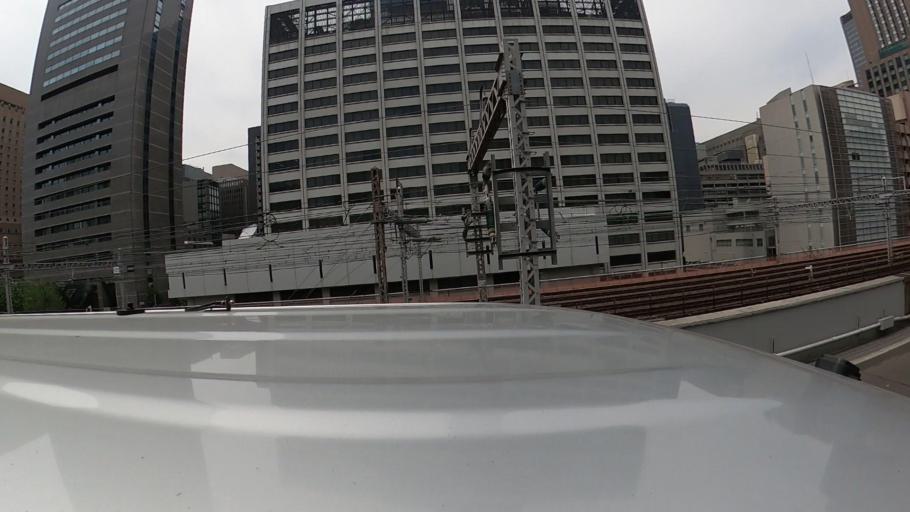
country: JP
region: Tokyo
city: Tokyo
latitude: 35.6699
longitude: 139.7591
